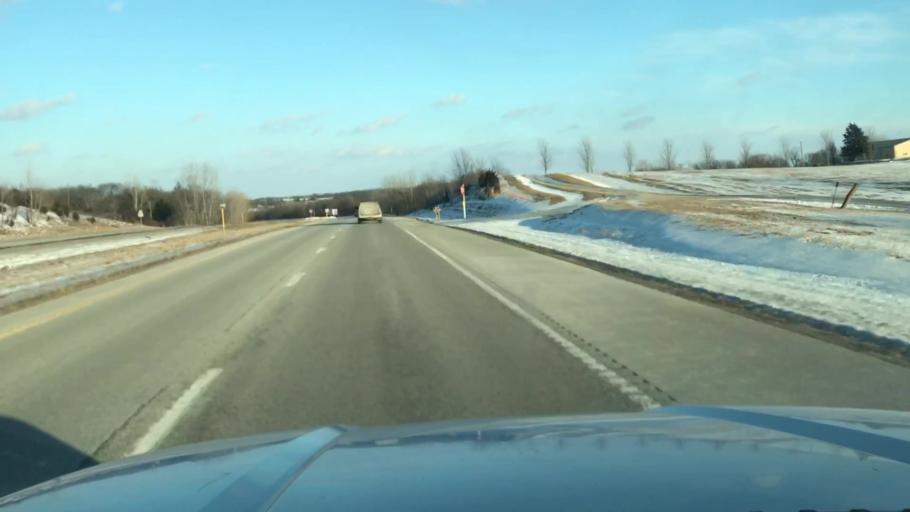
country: US
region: Missouri
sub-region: Clinton County
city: Gower
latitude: 39.7470
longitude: -94.6119
